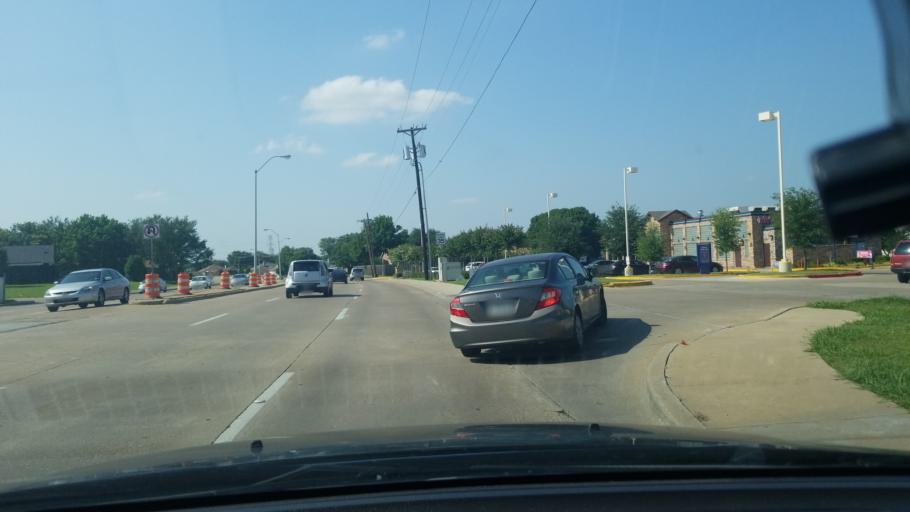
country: US
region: Texas
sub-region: Dallas County
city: Mesquite
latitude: 32.8119
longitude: -96.6110
